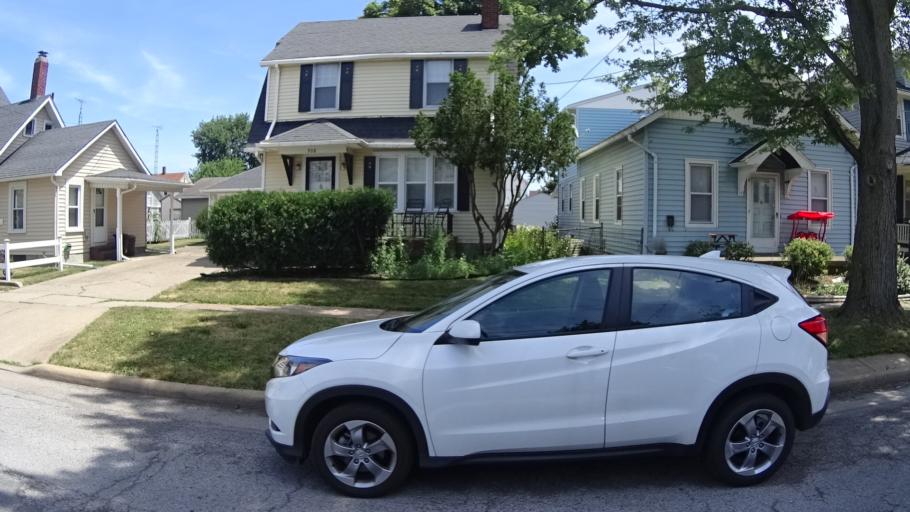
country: US
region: Ohio
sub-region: Erie County
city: Sandusky
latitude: 41.4467
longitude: -82.7175
